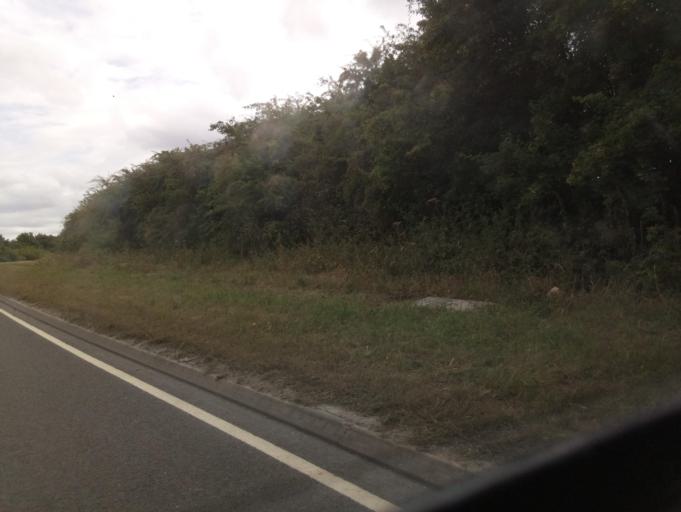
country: GB
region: England
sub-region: Leicestershire
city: Castle Donington
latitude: 52.8012
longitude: -1.3714
